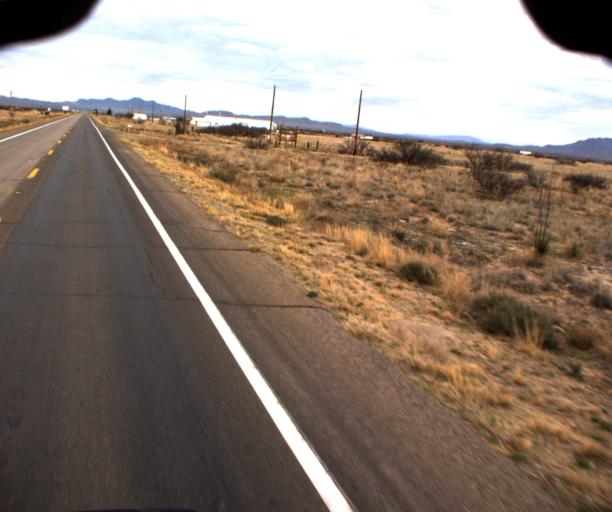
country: US
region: Arizona
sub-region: Cochise County
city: Willcox
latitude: 32.2263
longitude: -109.8660
